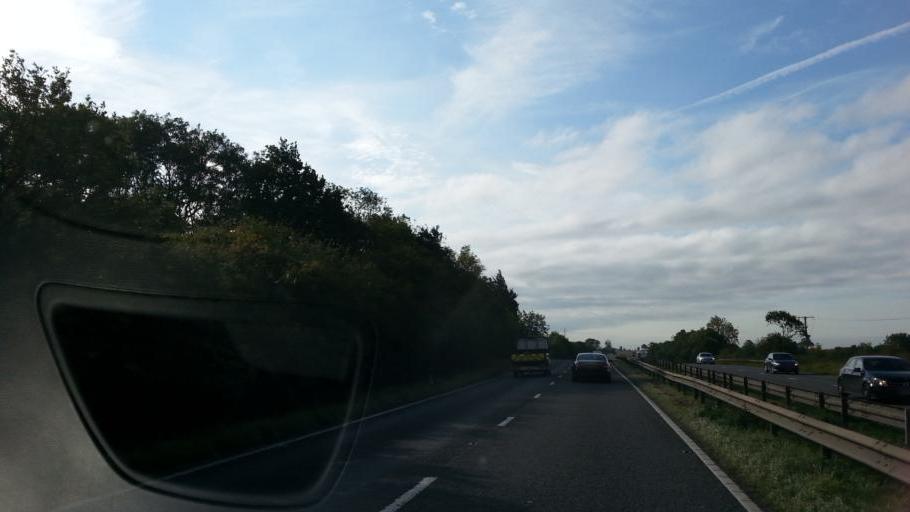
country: GB
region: England
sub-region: District of Rutland
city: Clipsham
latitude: 52.7949
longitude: -0.6105
